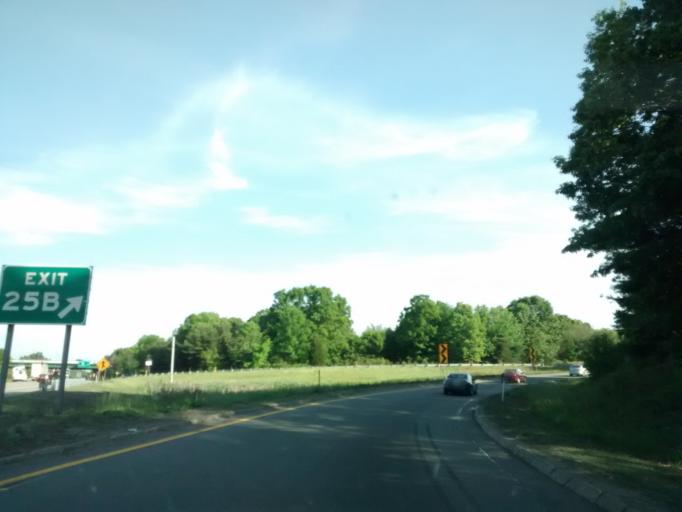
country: US
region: Massachusetts
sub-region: Middlesex County
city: Hudson
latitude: 42.3652
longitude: -71.5931
